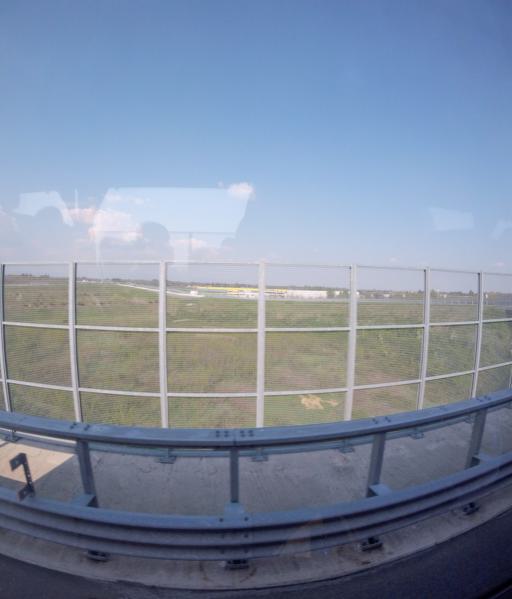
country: IT
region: Lombardy
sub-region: Provincia di Varese
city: Cassano Magnago
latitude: 45.6435
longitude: 8.8378
